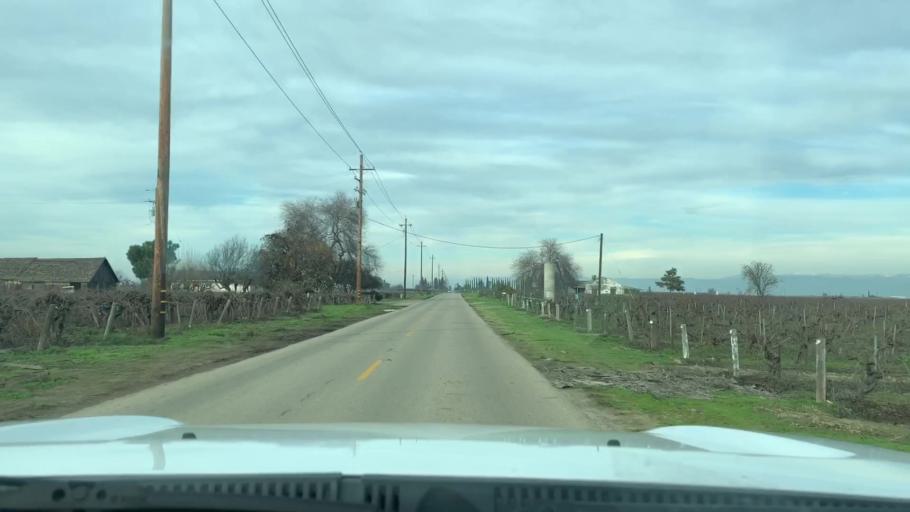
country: US
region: California
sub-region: Fresno County
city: Selma
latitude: 36.5937
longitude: -119.5748
